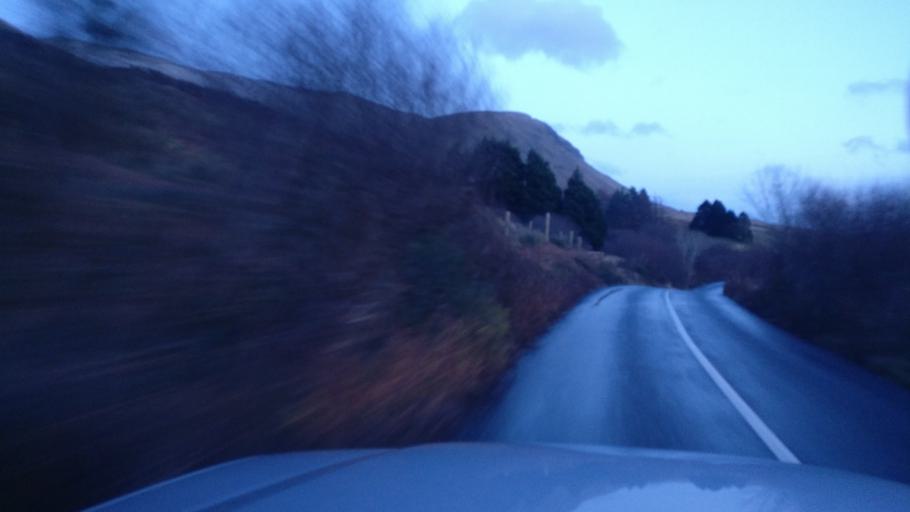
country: IE
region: Connaught
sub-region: Maigh Eo
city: Westport
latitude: 53.5537
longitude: -9.6369
